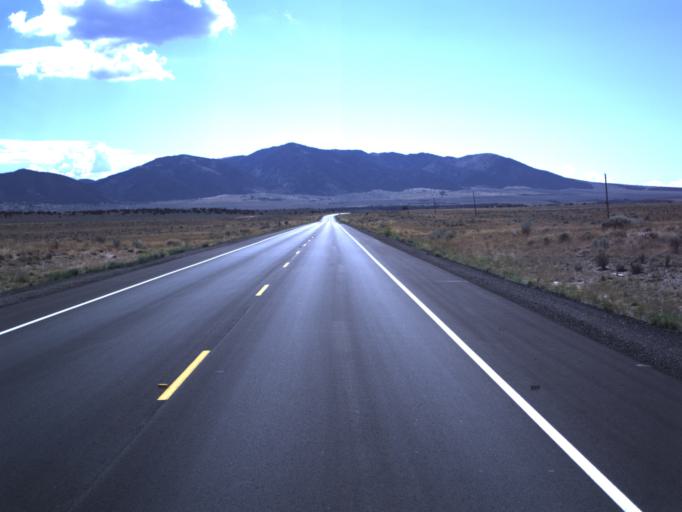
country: US
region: Utah
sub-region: Utah County
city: Eagle Mountain
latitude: 40.0594
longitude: -112.3102
